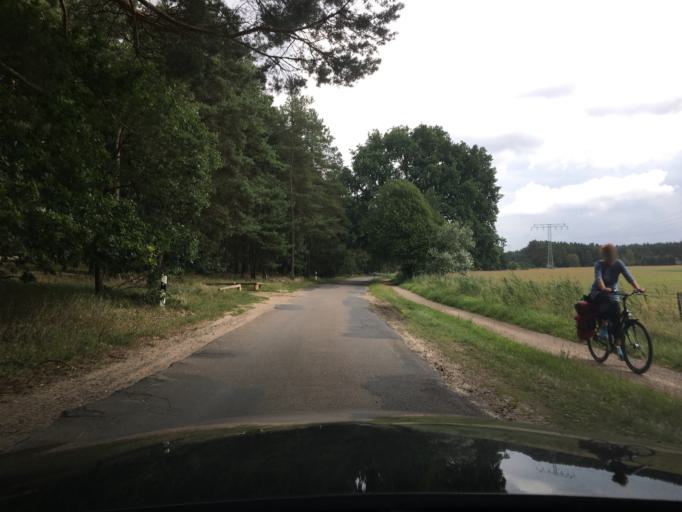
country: DE
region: Mecklenburg-Vorpommern
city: Mollenhagen
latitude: 53.4620
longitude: 12.8088
